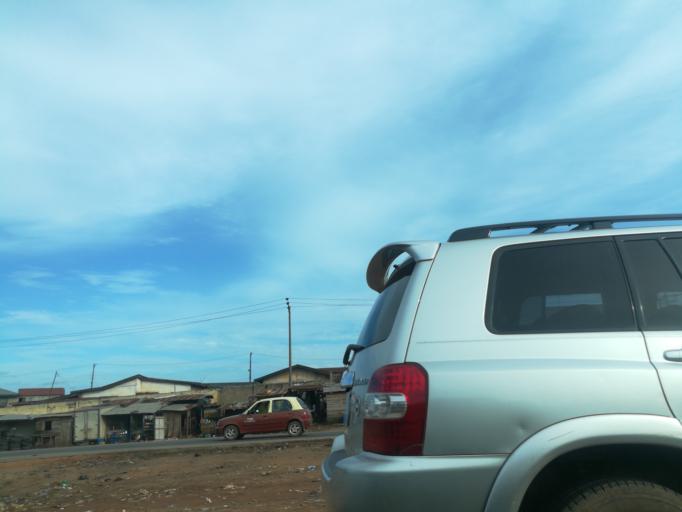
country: NG
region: Oyo
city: Ibadan
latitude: 7.3830
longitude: 3.9329
